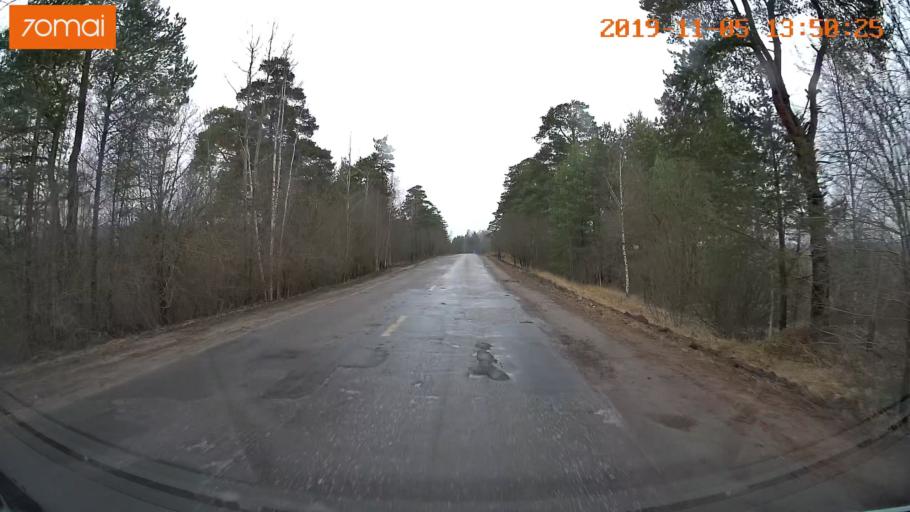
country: RU
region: Ivanovo
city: Kaminskiy
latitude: 57.0192
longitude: 41.4081
